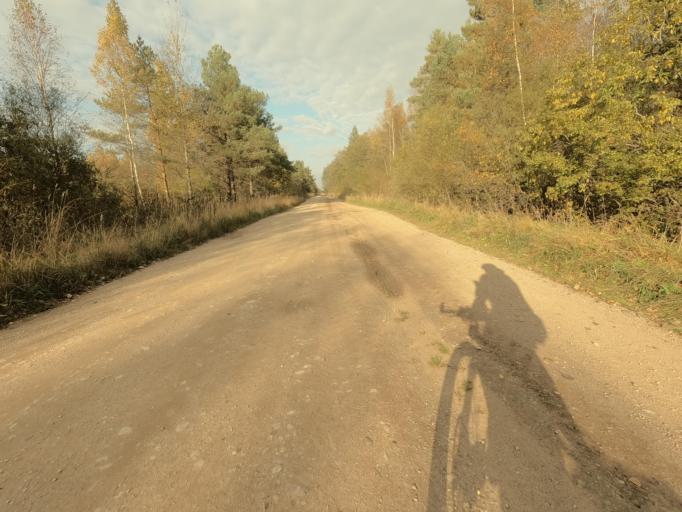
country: RU
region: Novgorod
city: Volkhovskiy
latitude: 58.8976
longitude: 31.0311
